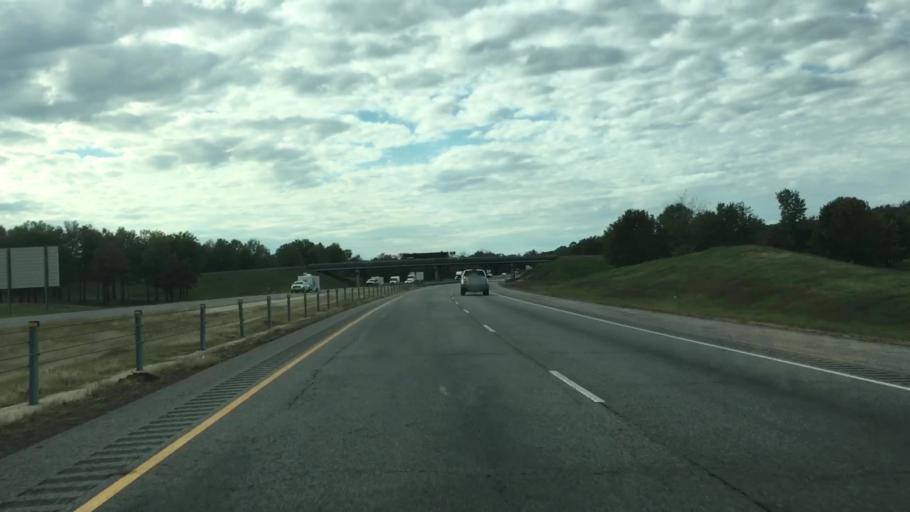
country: US
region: Arkansas
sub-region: Conway County
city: Morrilton
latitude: 35.1747
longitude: -92.7417
